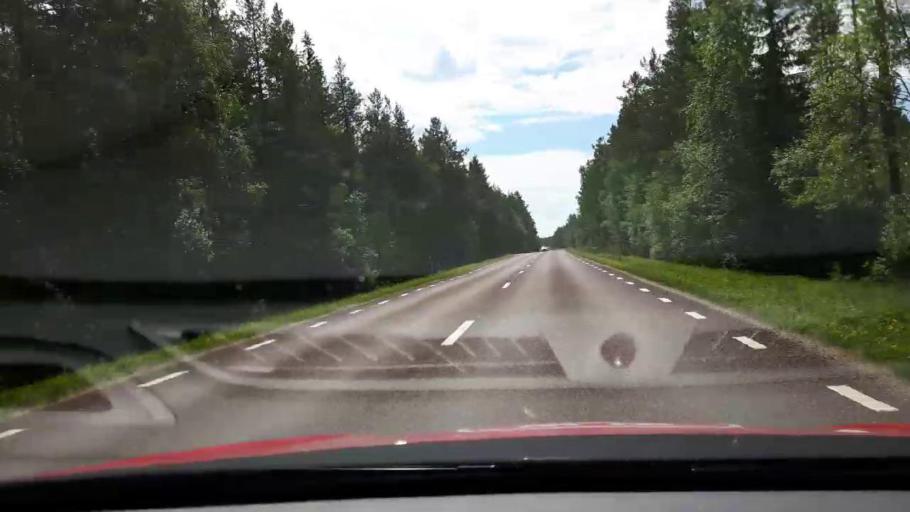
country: SE
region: Jaemtland
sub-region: Harjedalens Kommun
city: Sveg
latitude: 62.1145
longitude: 14.9703
